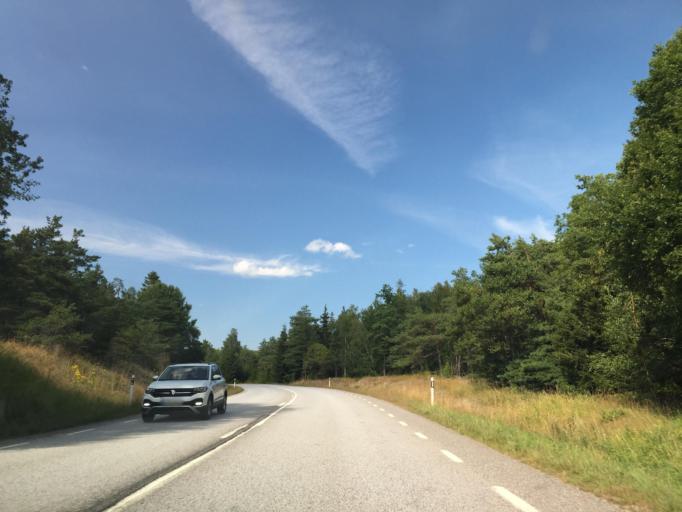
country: SE
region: Vaestra Goetaland
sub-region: Tanums Kommun
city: Tanumshede
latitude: 58.8167
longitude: 11.2630
